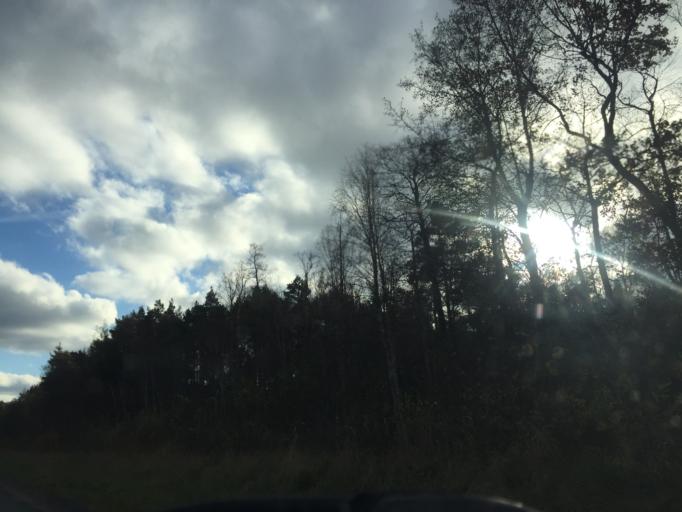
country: LV
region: Liepaja
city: Vec-Liepaja
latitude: 56.5772
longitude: 21.0429
